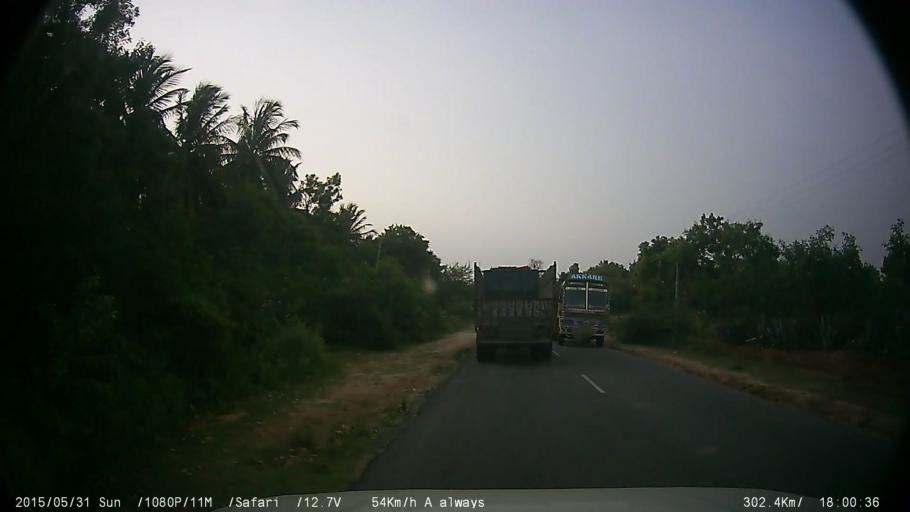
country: IN
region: Karnataka
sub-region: Mysore
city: Nanjangud
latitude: 12.0224
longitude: 76.6731
